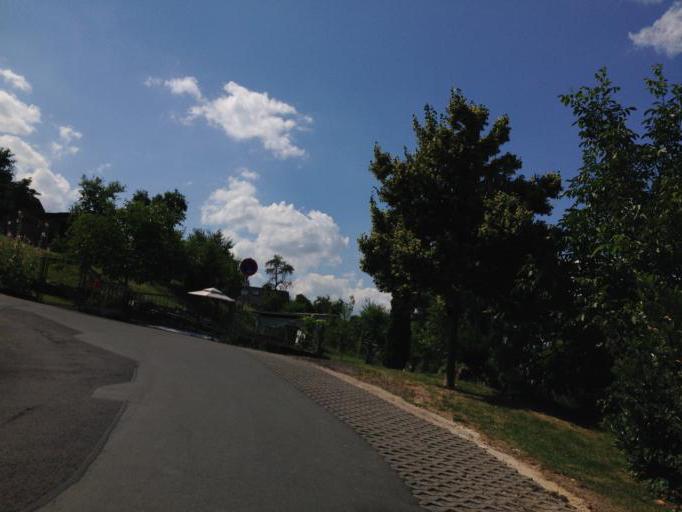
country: DE
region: Hesse
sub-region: Regierungsbezirk Giessen
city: Heuchelheim
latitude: 50.6160
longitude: 8.6371
